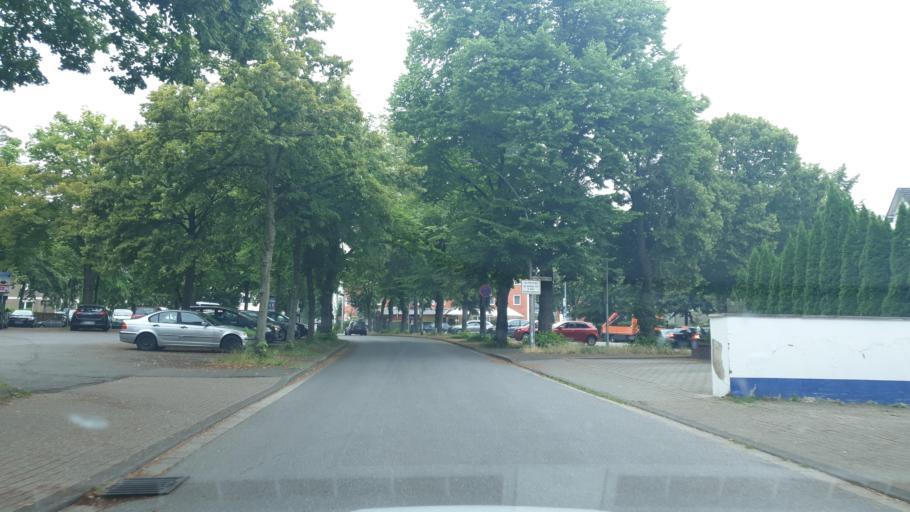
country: DE
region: North Rhine-Westphalia
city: Bad Oeynhausen
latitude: 52.2033
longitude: 8.7903
